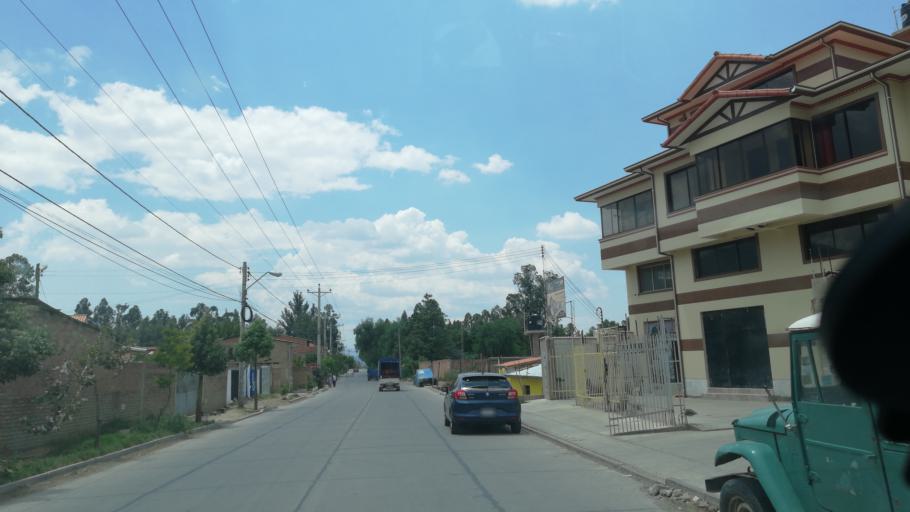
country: BO
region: Cochabamba
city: Cochabamba
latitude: -17.3631
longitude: -66.2228
